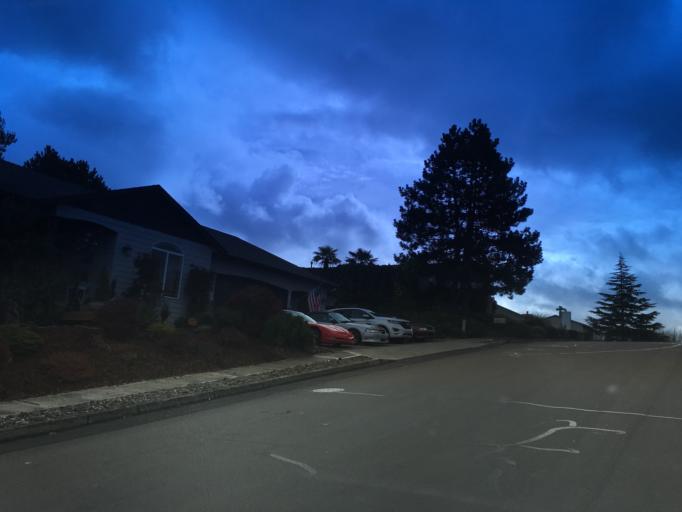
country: US
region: Oregon
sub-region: Multnomah County
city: Fairview
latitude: 45.5357
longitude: -122.4448
